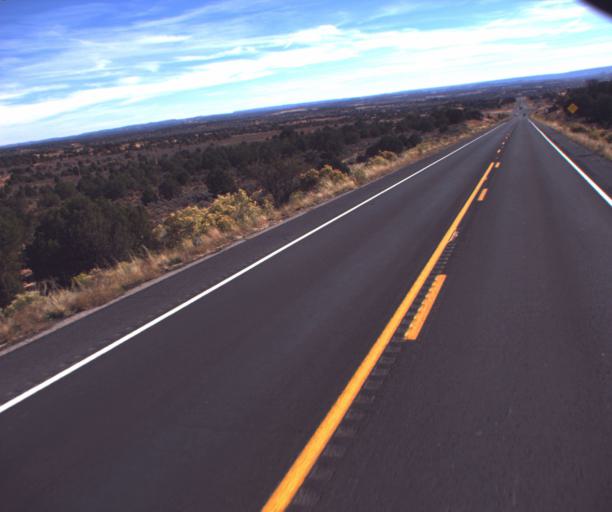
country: US
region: Arizona
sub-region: Coconino County
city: Kaibito
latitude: 36.5820
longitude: -110.8027
